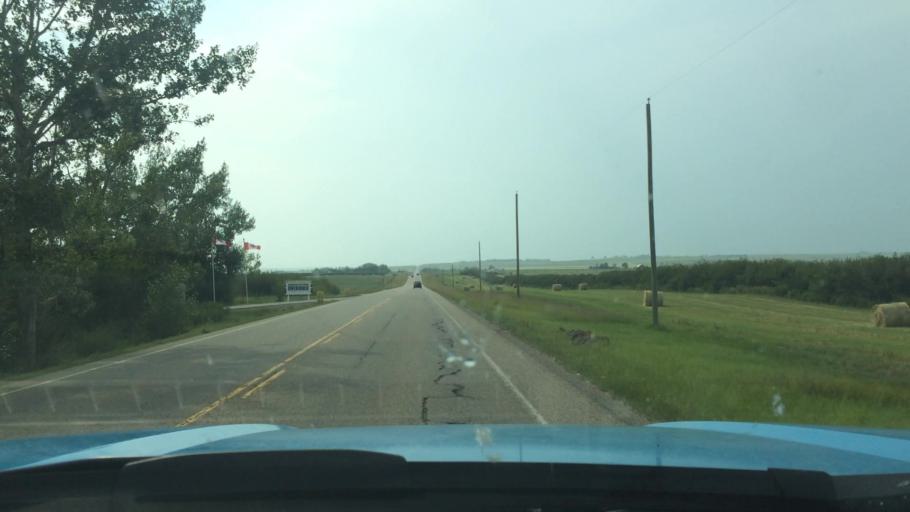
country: CA
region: Alberta
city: Airdrie
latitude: 51.2126
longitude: -114.0581
